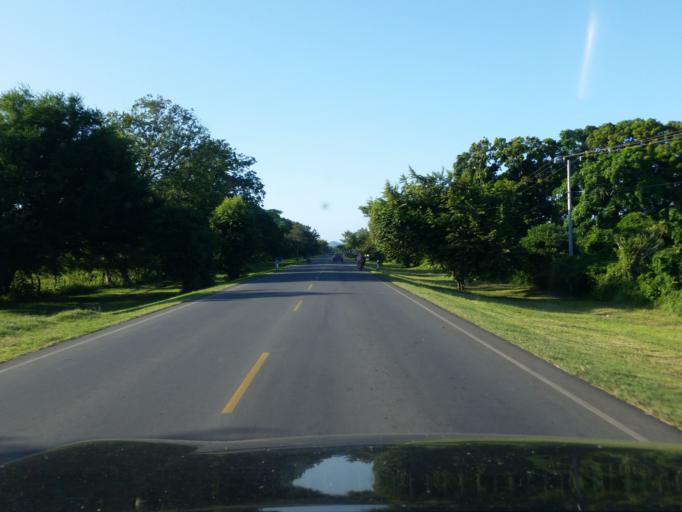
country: NI
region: Rivas
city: Potosi
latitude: 11.4885
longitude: -85.8715
